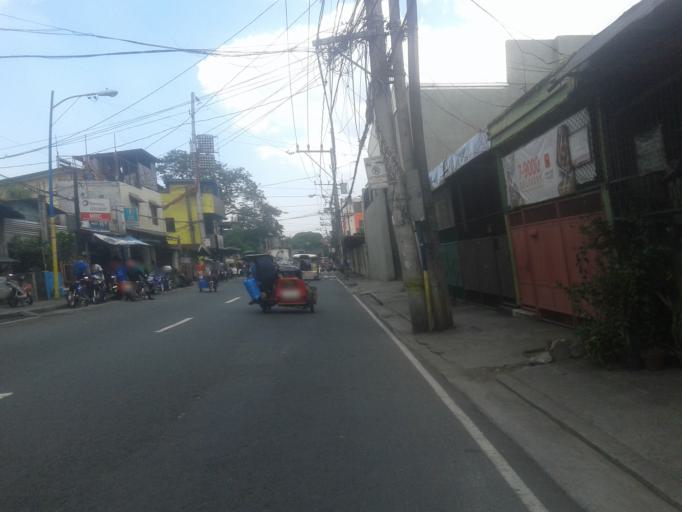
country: PH
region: Metro Manila
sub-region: Mandaluyong
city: Mandaluyong City
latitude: 14.5876
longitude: 121.0394
